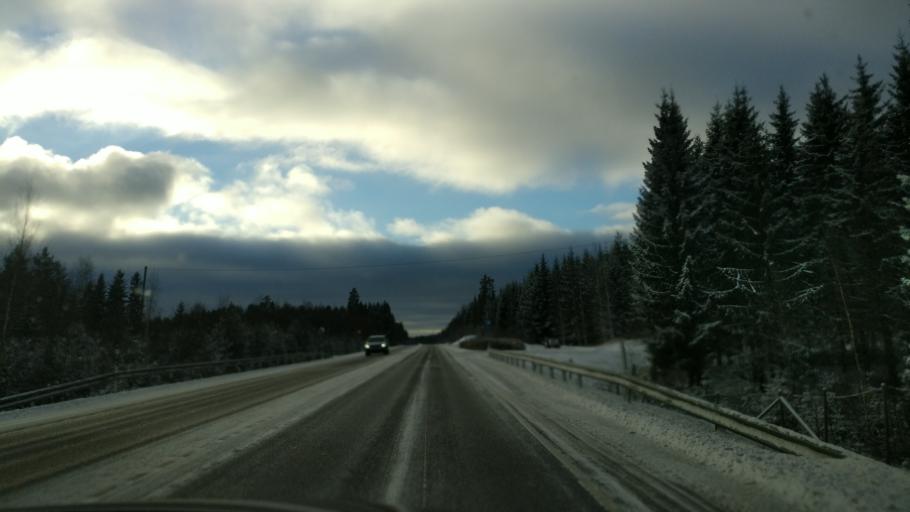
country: FI
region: Paijanne Tavastia
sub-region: Lahti
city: Heinola
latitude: 61.3470
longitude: 26.2069
